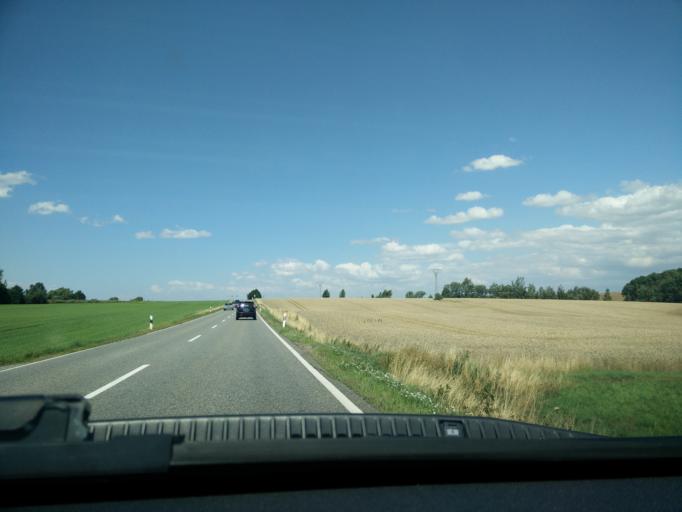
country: DE
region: Saxony
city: Narsdorf
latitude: 50.9783
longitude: 12.6983
